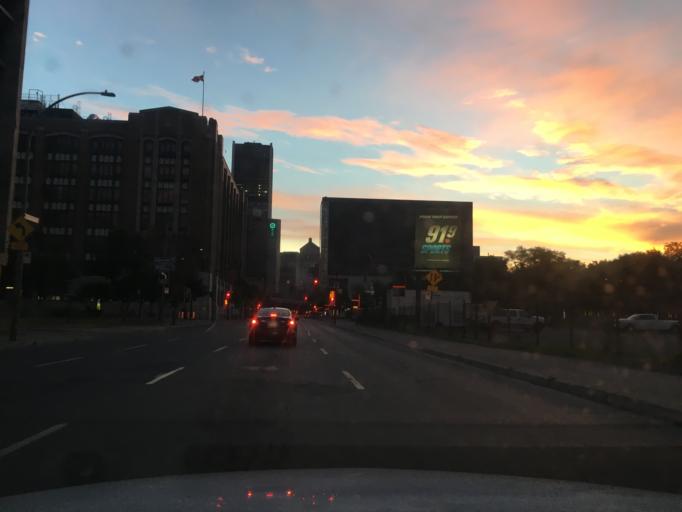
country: CA
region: Quebec
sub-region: Montreal
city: Montreal
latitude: 45.4955
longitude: -73.5660
